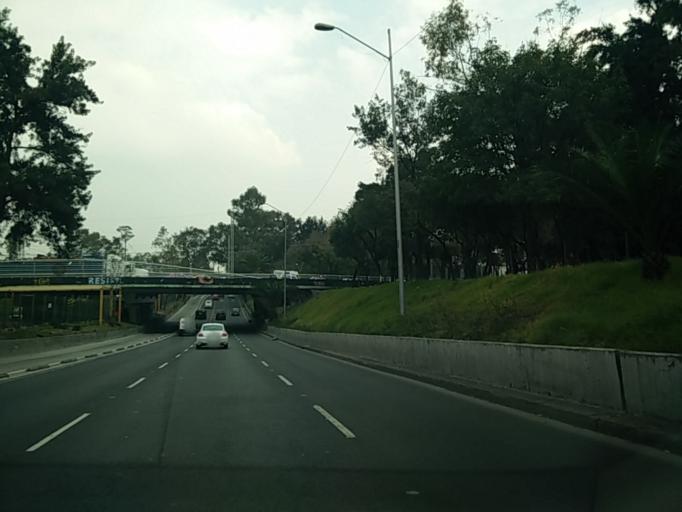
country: MX
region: Mexico
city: Colonia Lindavista
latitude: 19.4808
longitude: -99.1289
